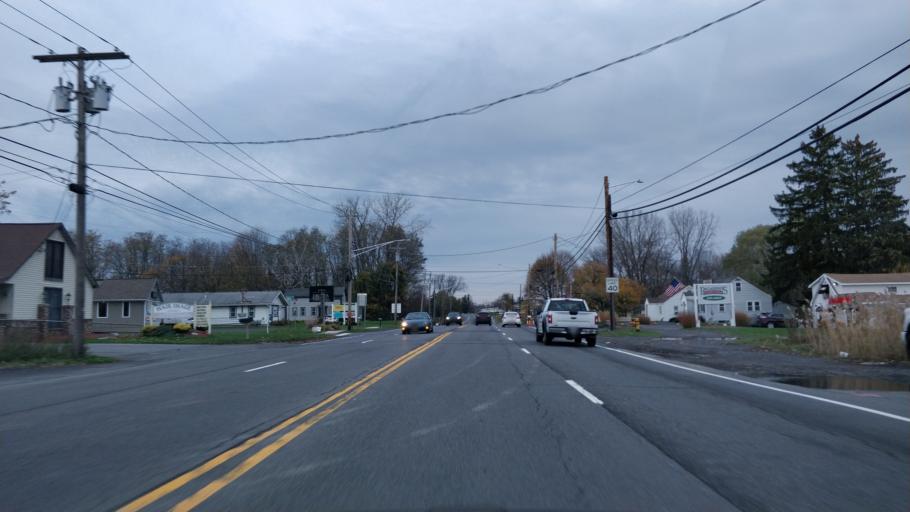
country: US
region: New York
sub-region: Onondaga County
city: North Syracuse
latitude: 43.1650
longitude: -76.1190
